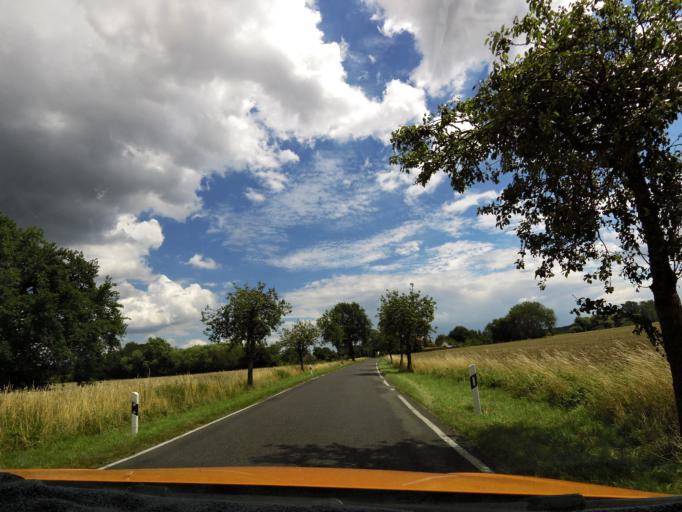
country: DE
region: Brandenburg
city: Storkow
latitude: 52.2475
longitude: 13.8930
